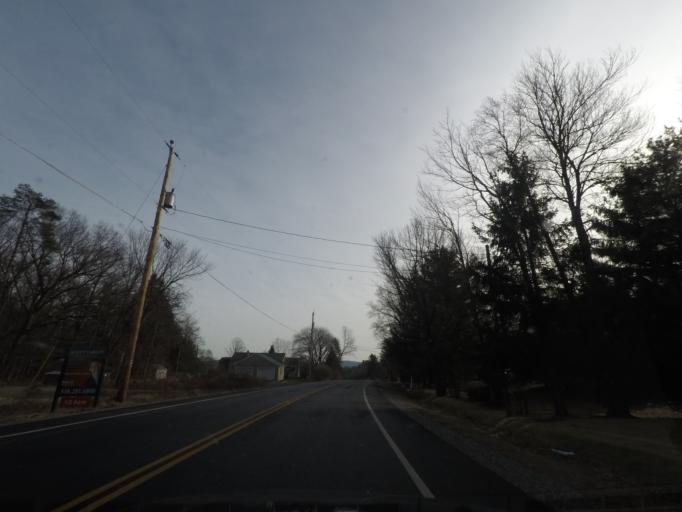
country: US
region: New York
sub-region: Saratoga County
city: Mechanicville
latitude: 42.8622
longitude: -73.6922
